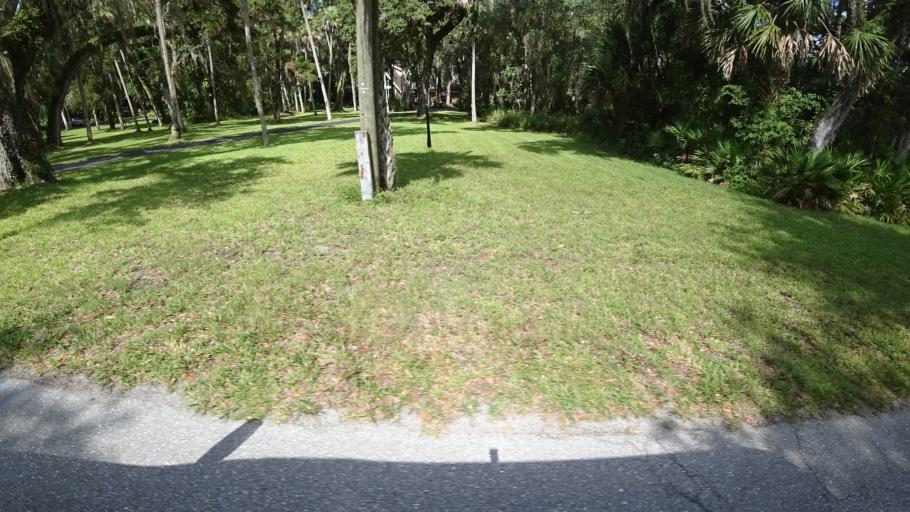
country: US
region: Florida
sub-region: Manatee County
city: Samoset
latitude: 27.4651
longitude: -82.4785
